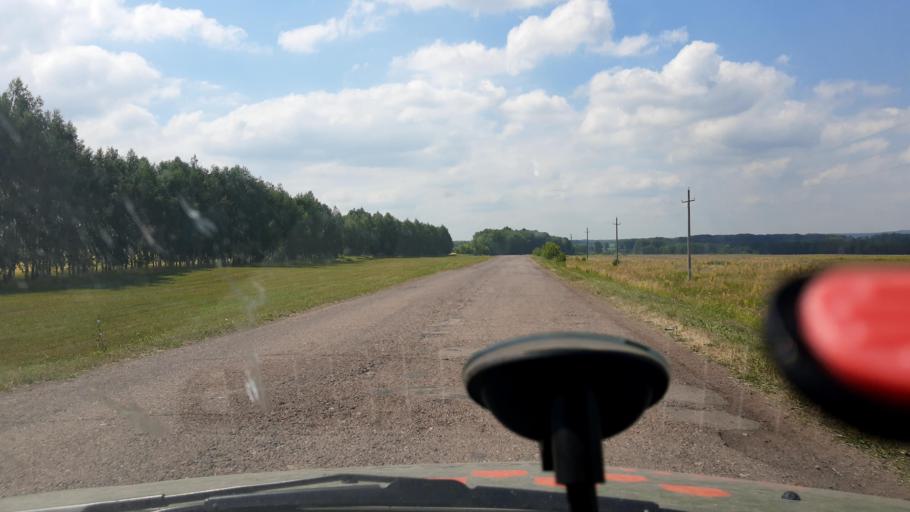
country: RU
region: Bashkortostan
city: Chekmagush
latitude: 54.8844
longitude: 54.5951
